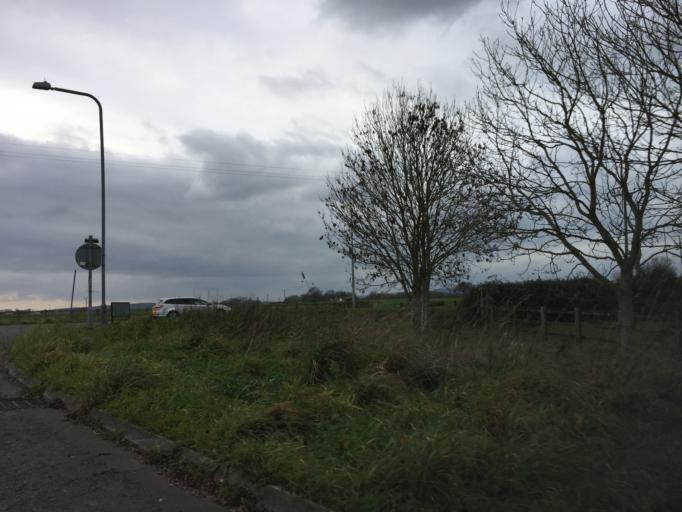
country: GB
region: Wales
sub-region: Monmouthshire
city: Caldicot
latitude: 51.6102
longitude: -2.7148
